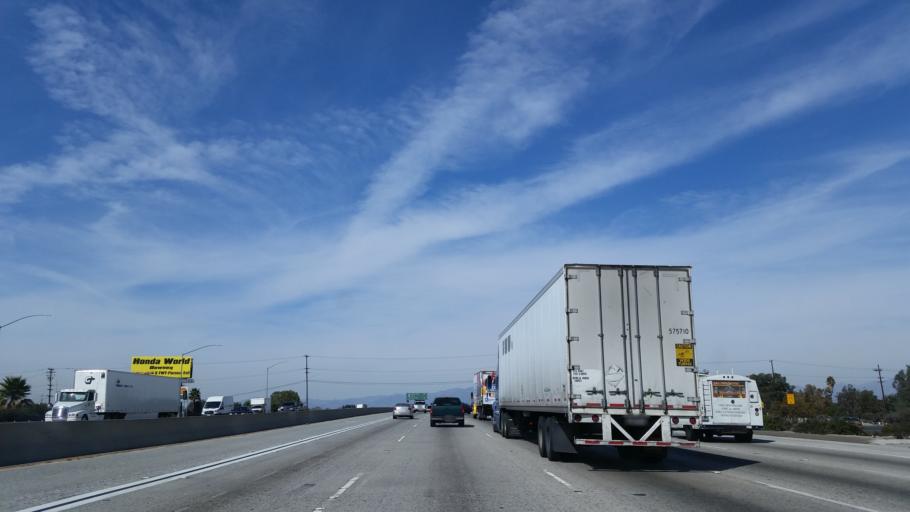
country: US
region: California
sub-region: Los Angeles County
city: Bellflower
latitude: 33.8850
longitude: -118.1042
